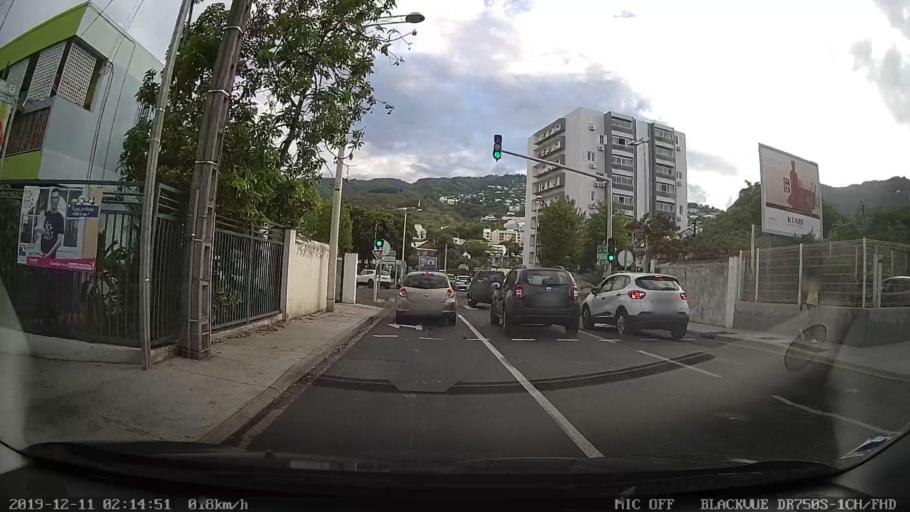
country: RE
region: Reunion
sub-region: Reunion
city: Saint-Denis
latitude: -20.8897
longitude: 55.4531
